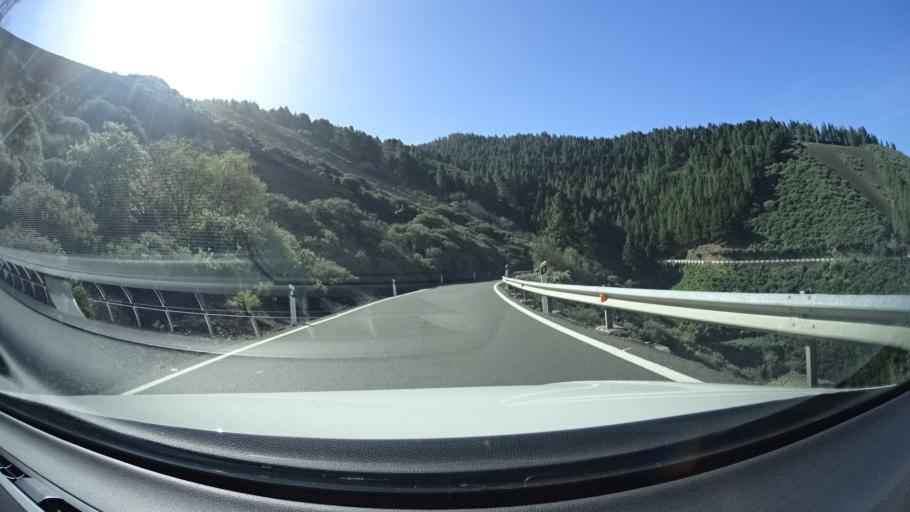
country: ES
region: Canary Islands
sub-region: Provincia de Las Palmas
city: Artenara
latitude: 28.0278
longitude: -15.6178
